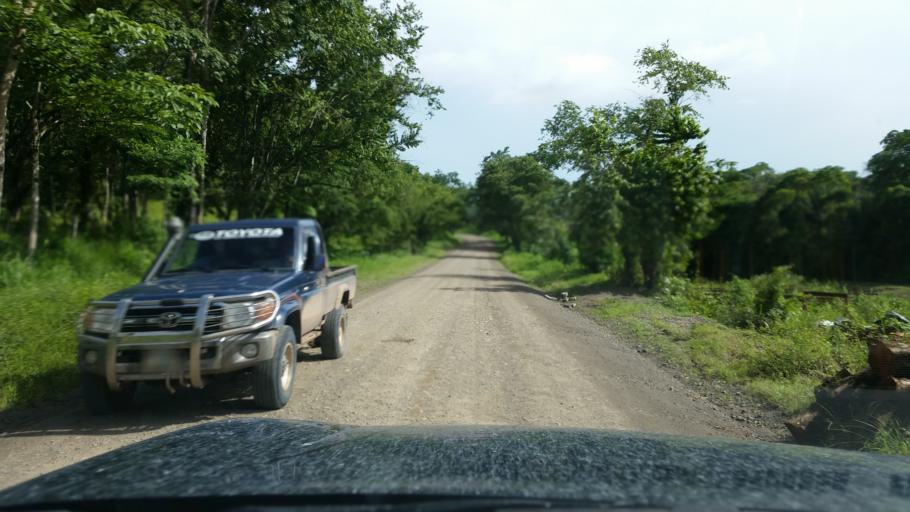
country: NI
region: Atlantico Norte (RAAN)
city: Siuna
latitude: 13.6705
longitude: -84.7917
